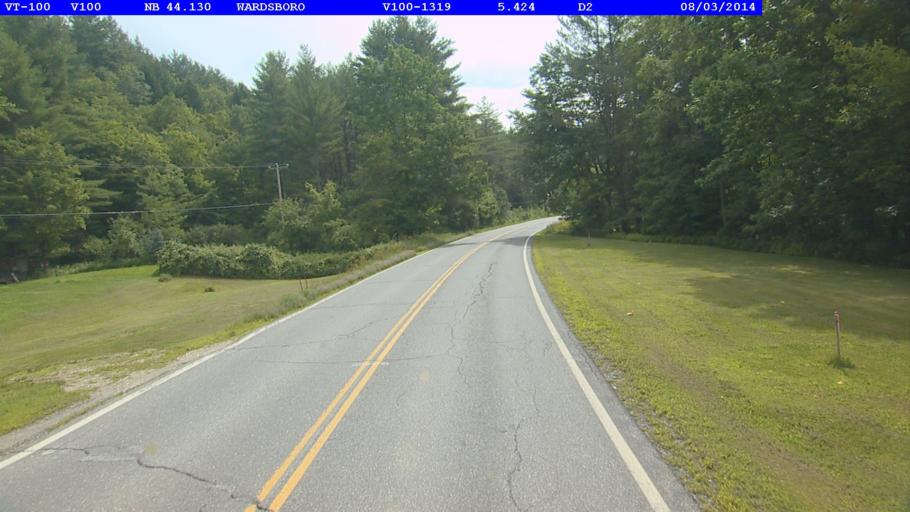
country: US
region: Vermont
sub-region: Windham County
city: Dover
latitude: 43.0345
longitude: -72.8056
